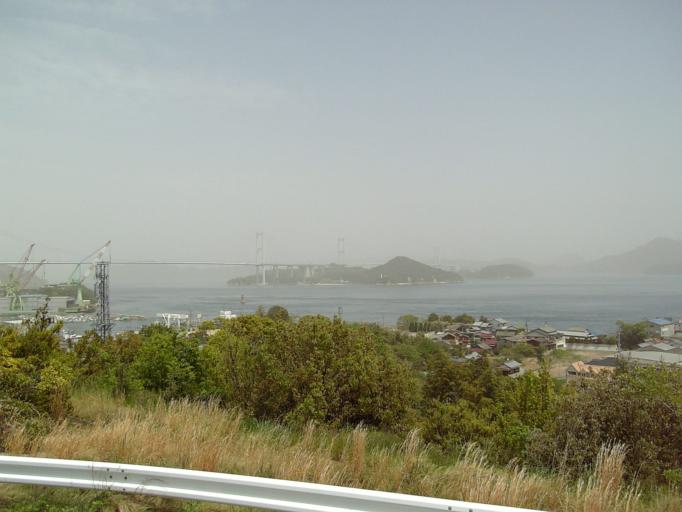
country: JP
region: Ehime
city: Hojo
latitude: 34.1001
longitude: 132.9786
